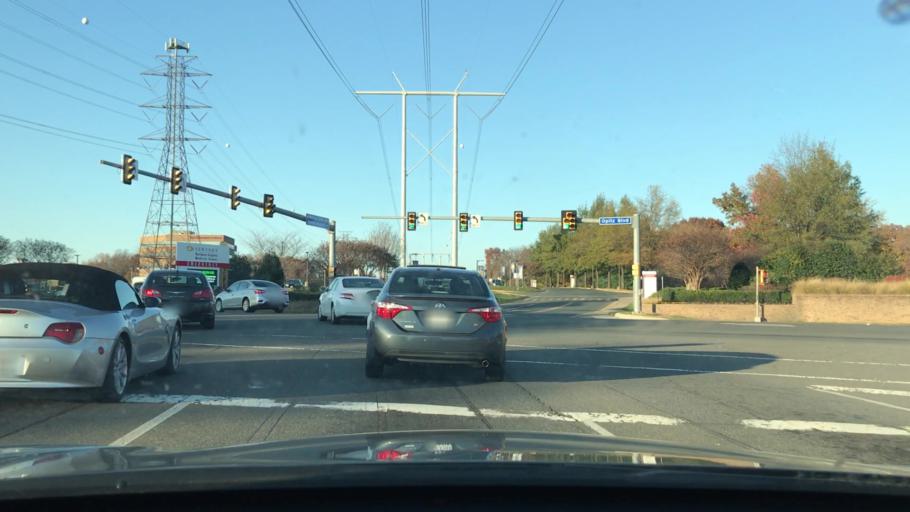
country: US
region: Virginia
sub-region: Prince William County
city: Potomac Mills
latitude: 38.6344
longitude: -77.2842
